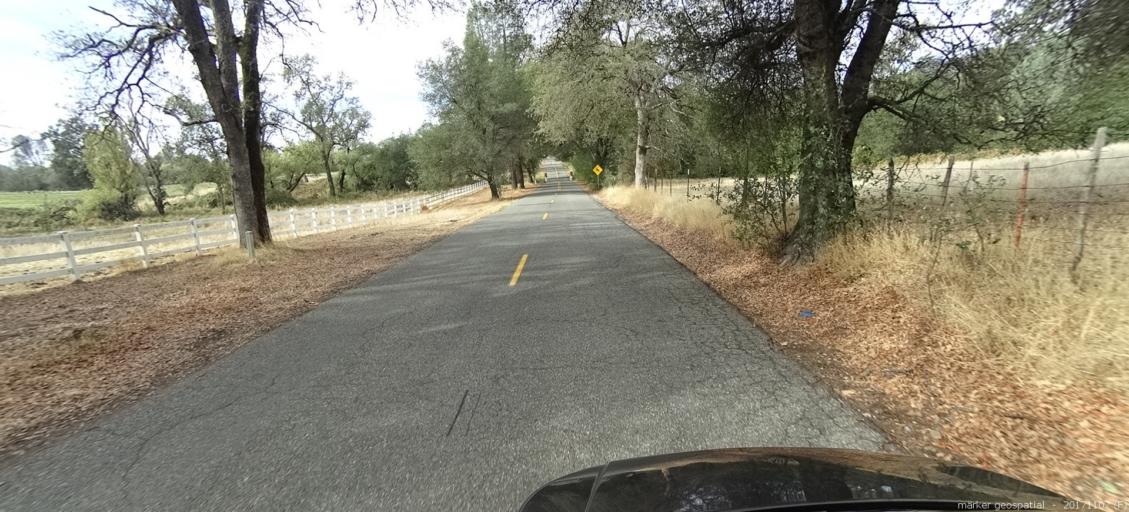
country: US
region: California
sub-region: Shasta County
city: Shasta
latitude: 40.5012
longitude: -122.5665
